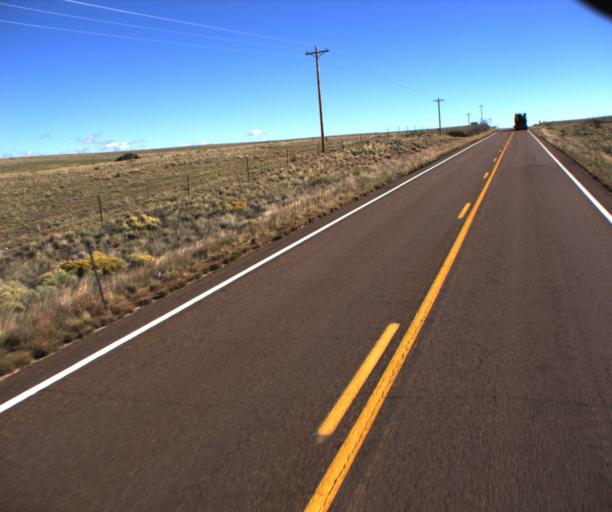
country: US
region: Arizona
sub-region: Apache County
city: Saint Johns
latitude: 34.5049
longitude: -109.4814
